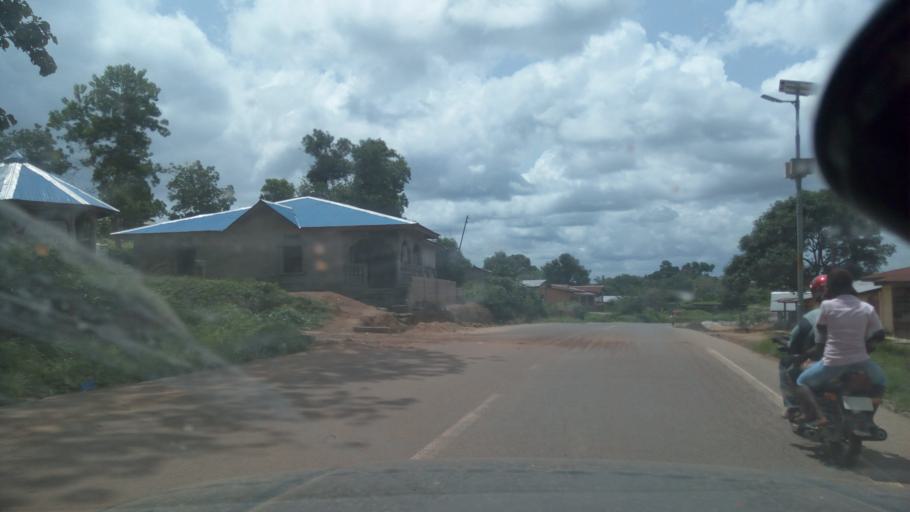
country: SL
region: Eastern Province
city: Kenema
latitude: 7.8771
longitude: -11.1705
